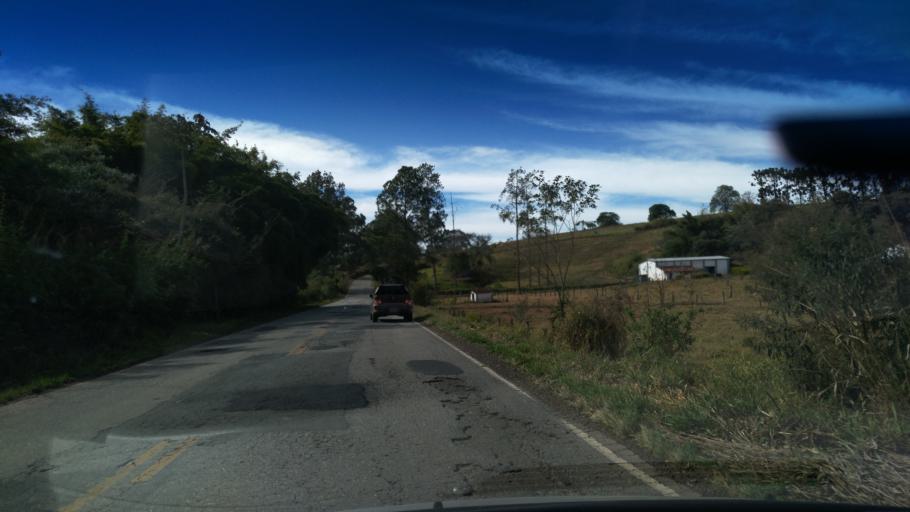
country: BR
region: Minas Gerais
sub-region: Andradas
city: Andradas
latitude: -22.0662
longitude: -46.4664
